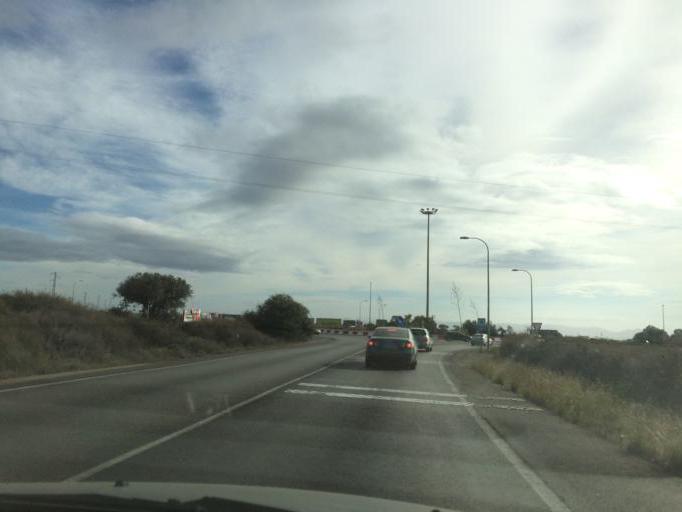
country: ES
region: Andalusia
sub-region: Provincia de Almeria
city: Retamar
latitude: 36.8555
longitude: -2.3463
